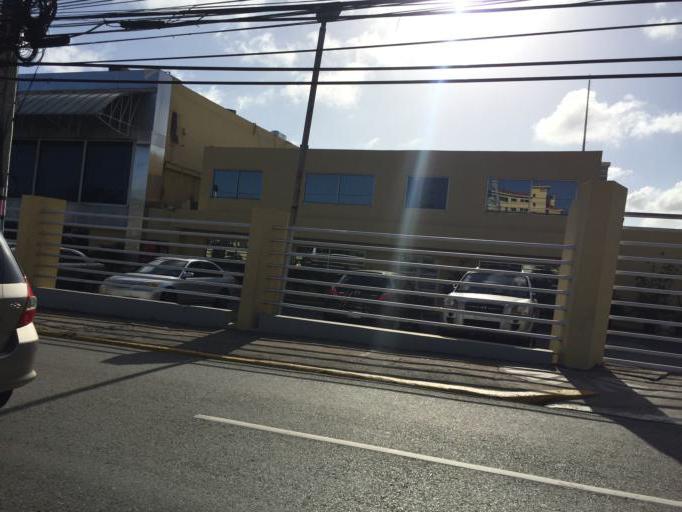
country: DO
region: Nacional
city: La Julia
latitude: 18.4626
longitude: -69.9287
